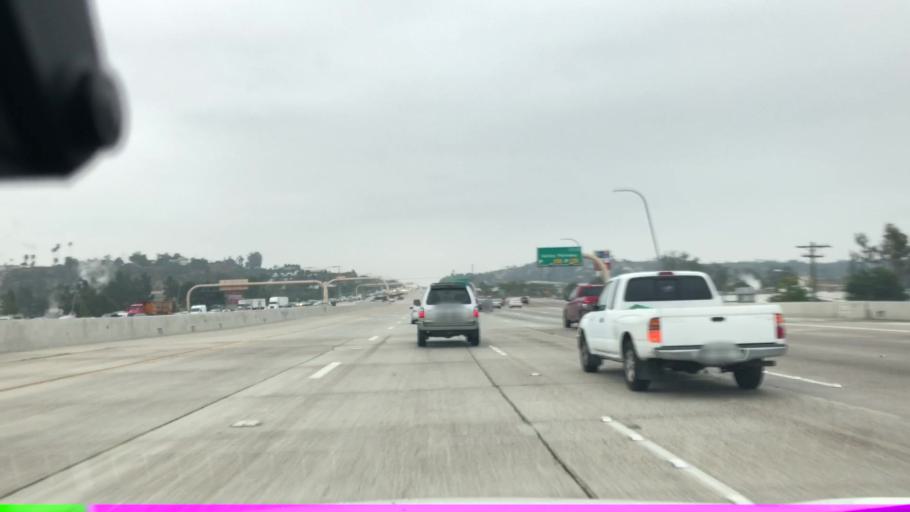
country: US
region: California
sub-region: San Diego County
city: Escondido
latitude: 33.1201
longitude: -117.1020
